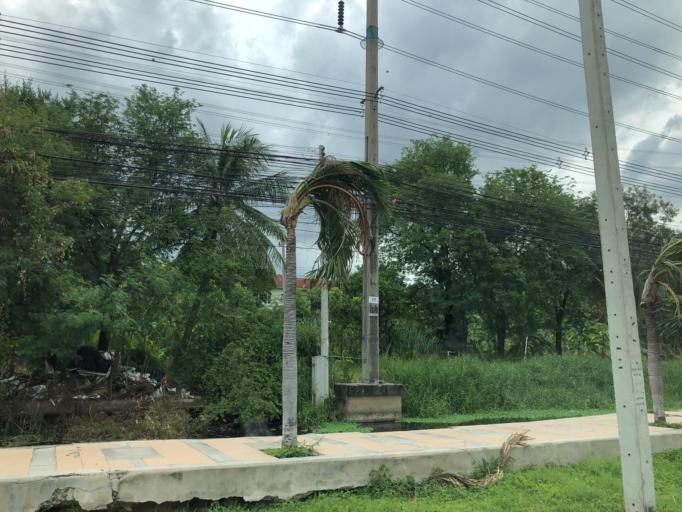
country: TH
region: Bangkok
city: Lak Si
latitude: 13.8890
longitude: 100.5527
